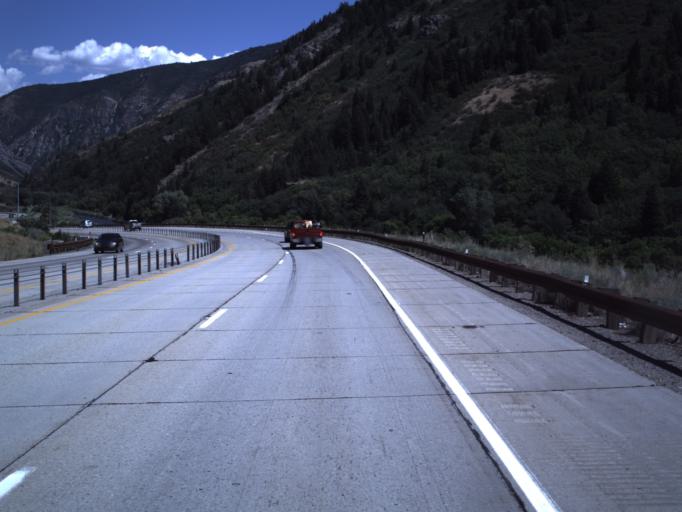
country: US
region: Utah
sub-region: Utah County
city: Orem
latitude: 40.3485
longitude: -111.5913
